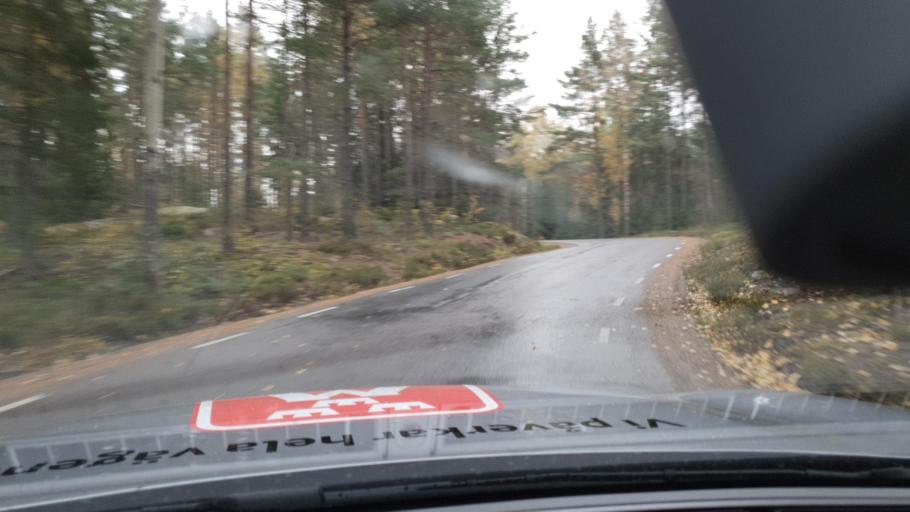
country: SE
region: Stockholm
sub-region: Sodertalje Kommun
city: Molnbo
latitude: 59.1144
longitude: 17.4221
